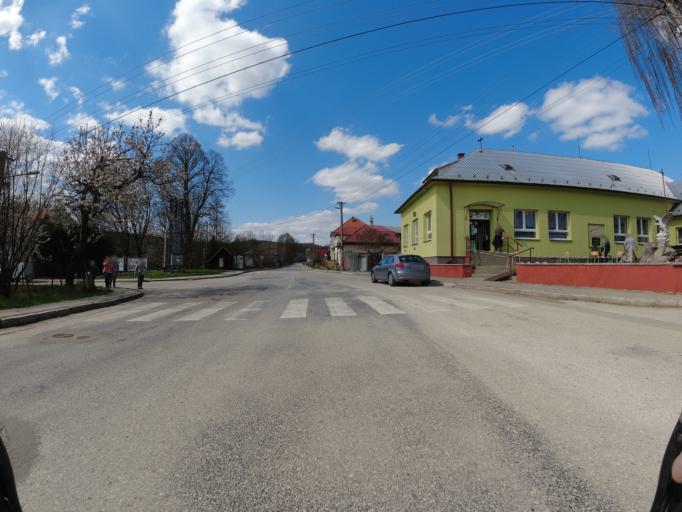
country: SK
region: Nitriansky
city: Stara Tura
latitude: 48.7406
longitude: 17.7238
